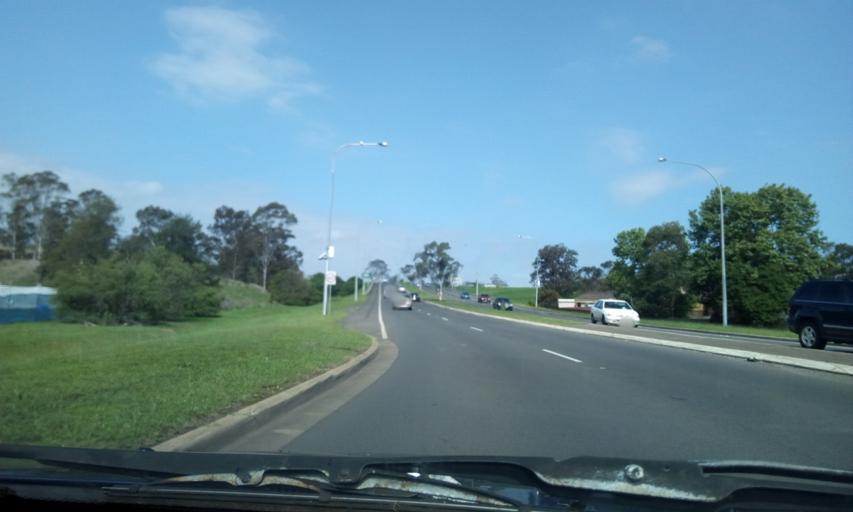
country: AU
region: New South Wales
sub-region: Campbelltown Municipality
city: Campbelltown
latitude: -34.0802
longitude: 150.8041
